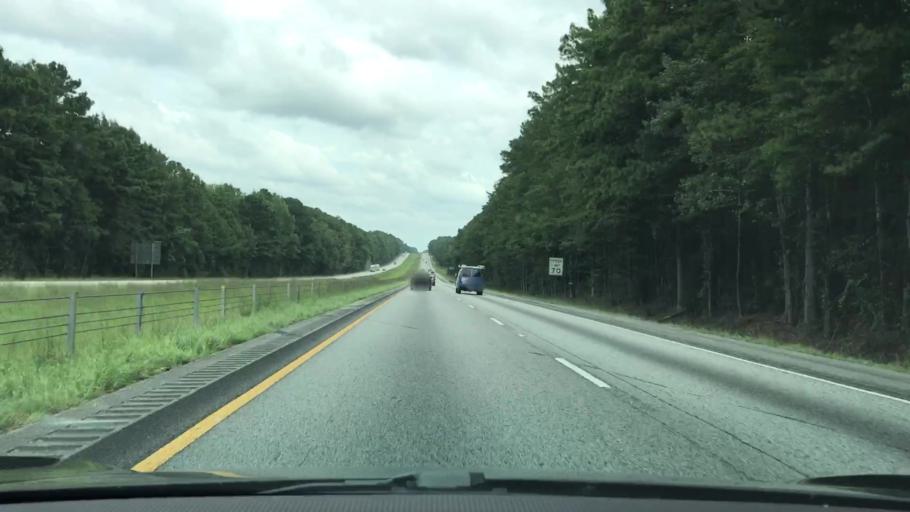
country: US
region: Alabama
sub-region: Chambers County
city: Huguley
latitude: 32.7542
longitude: -85.2739
